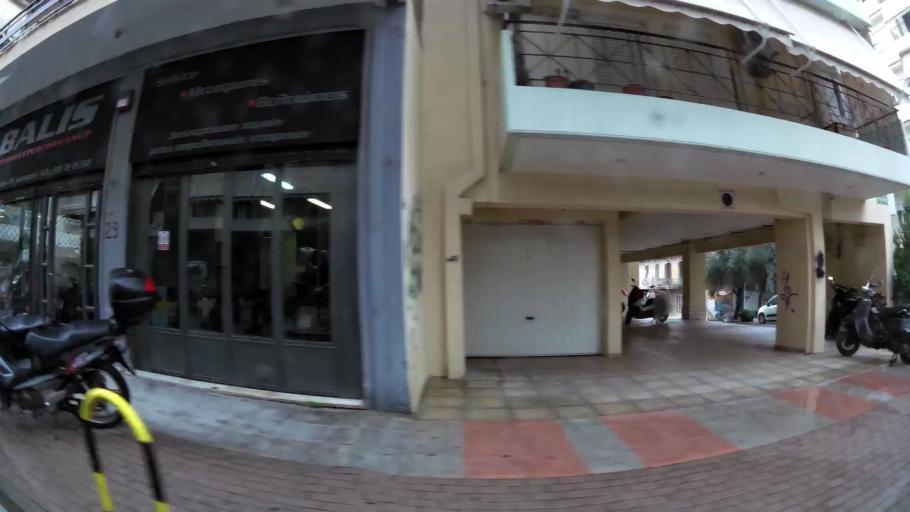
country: GR
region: Attica
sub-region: Nomarchia Athinas
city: Kaisariani
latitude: 37.9702
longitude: 23.7594
